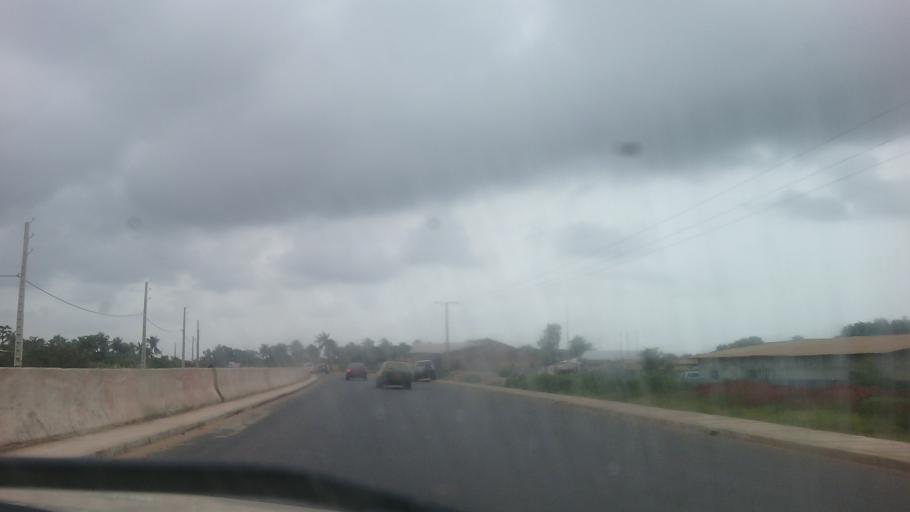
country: BJ
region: Atlantique
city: Ouidah
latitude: 6.3645
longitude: 2.0533
